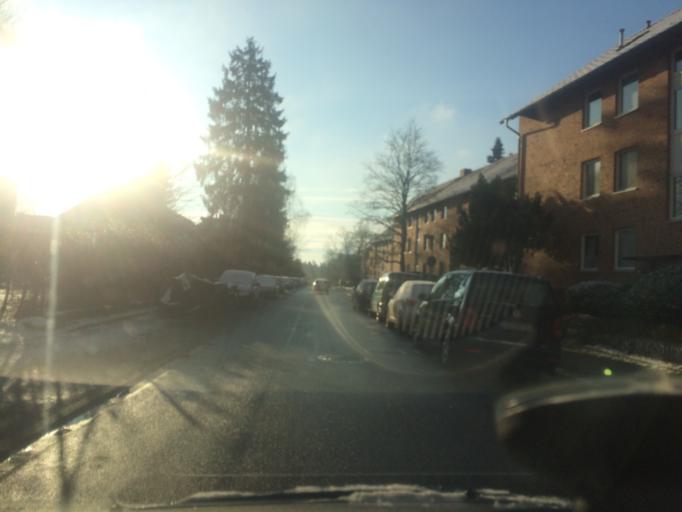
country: DE
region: Lower Saxony
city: Lueneburg
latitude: 53.2280
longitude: 10.3974
